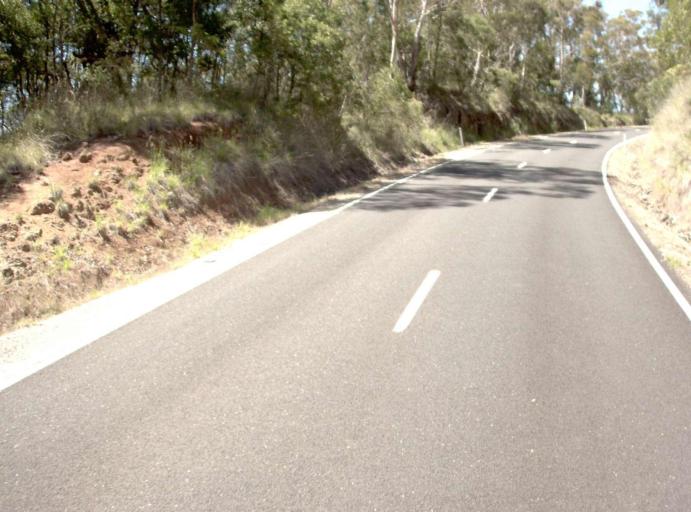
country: AU
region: Victoria
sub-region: East Gippsland
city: Lakes Entrance
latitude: -37.2422
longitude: 148.2559
